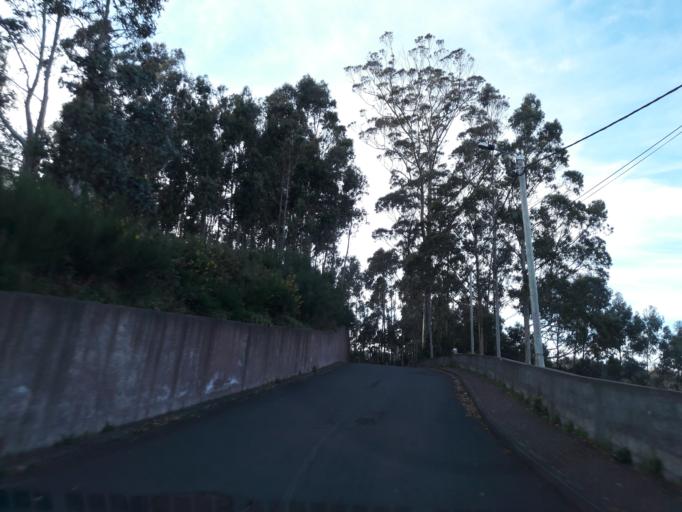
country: PT
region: Madeira
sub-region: Santa Cruz
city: Camacha
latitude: 32.6842
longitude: -16.8497
